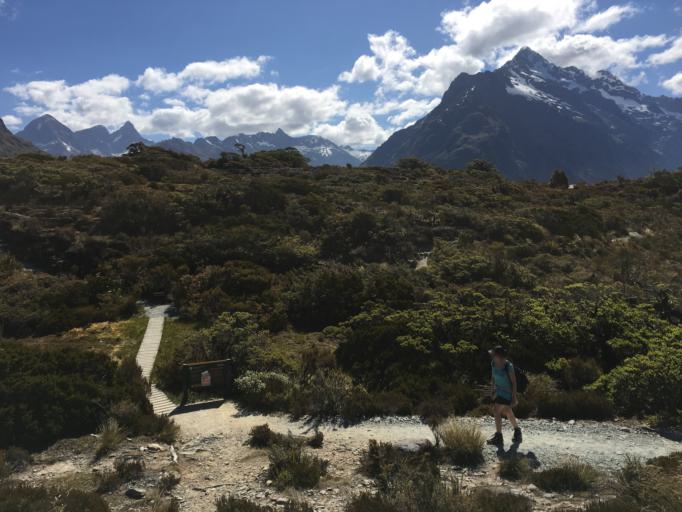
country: NZ
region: Otago
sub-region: Queenstown-Lakes District
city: Queenstown
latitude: -44.8141
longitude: 168.1289
